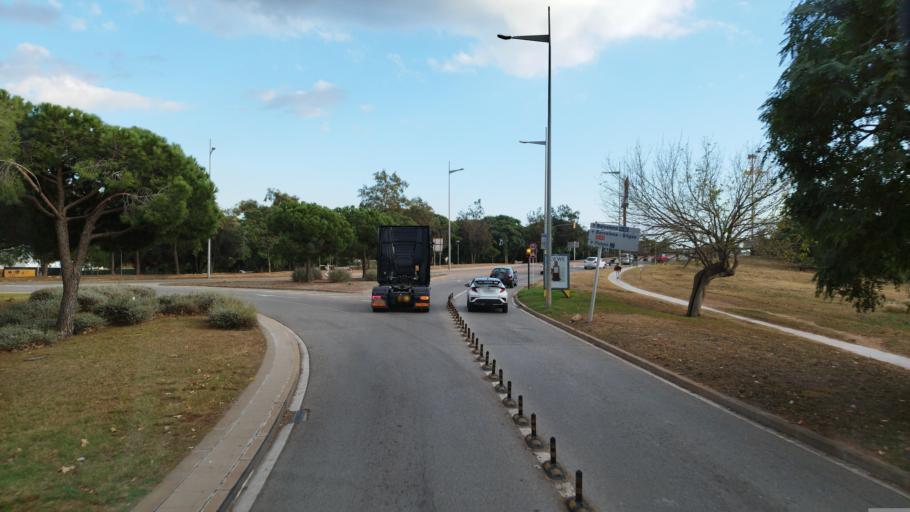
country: ES
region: Catalonia
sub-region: Provincia de Barcelona
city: Castelldefels
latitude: 41.2811
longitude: 1.9874
